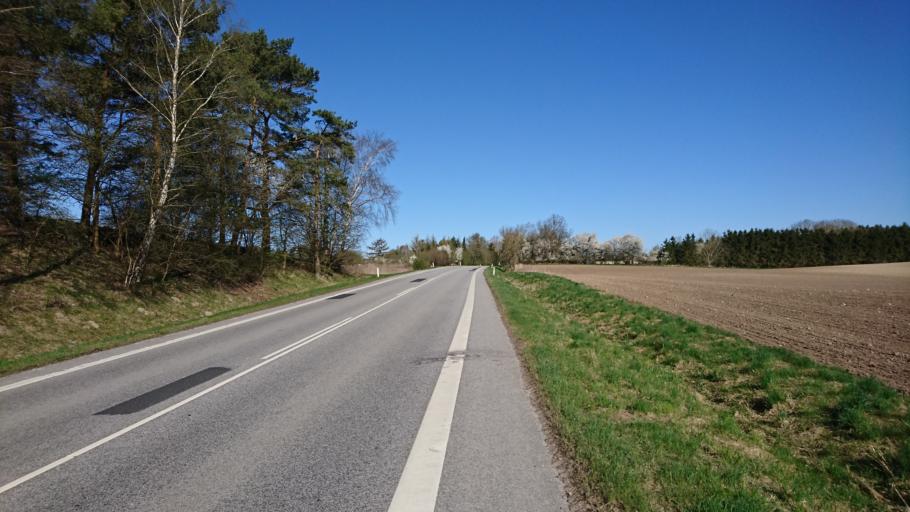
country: DK
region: Zealand
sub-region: Holbaek Kommune
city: Vipperod
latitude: 55.6920
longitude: 11.7887
